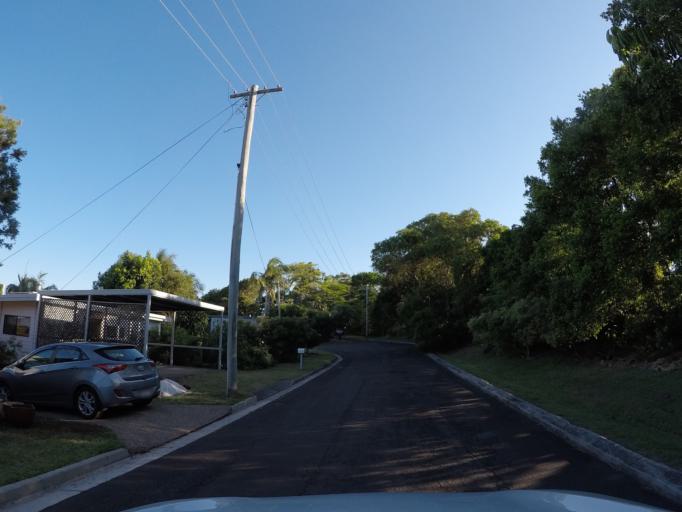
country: AU
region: Queensland
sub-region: Sunshine Coast
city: Nambour
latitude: -26.6368
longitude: 152.8698
